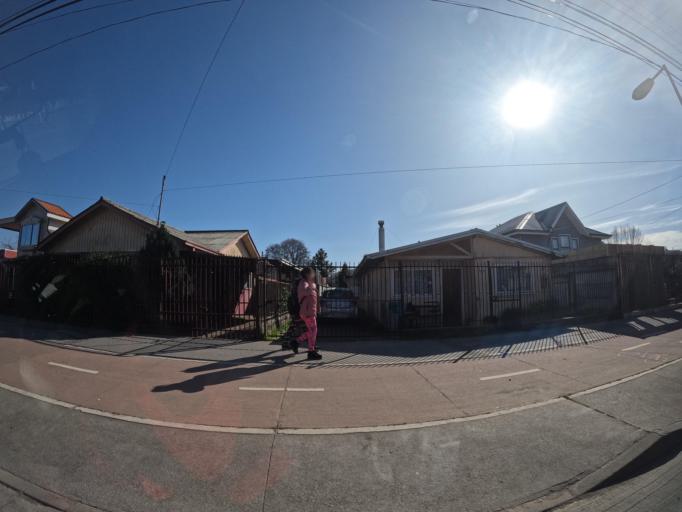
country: CL
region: Biobio
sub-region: Provincia de Concepcion
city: Chiguayante
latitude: -36.9709
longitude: -72.9364
